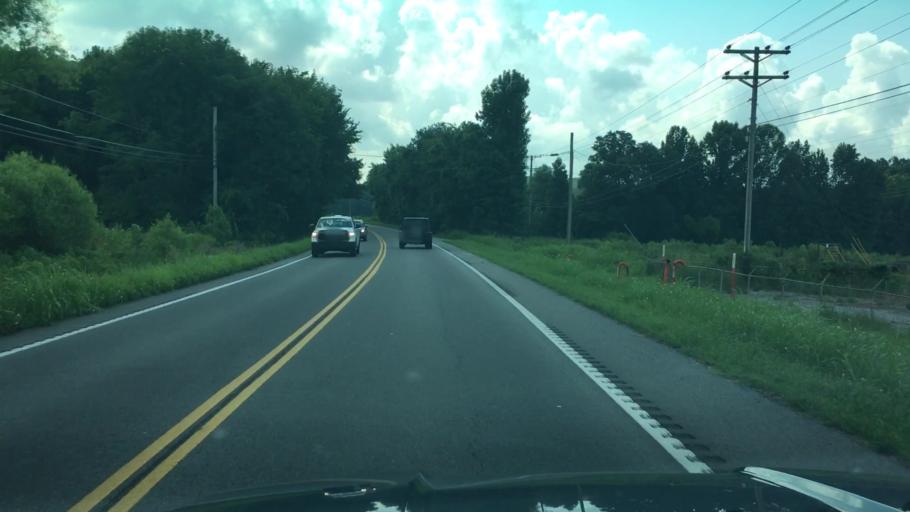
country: US
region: Tennessee
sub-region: Williamson County
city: Nolensville
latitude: 35.8597
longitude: -86.6814
